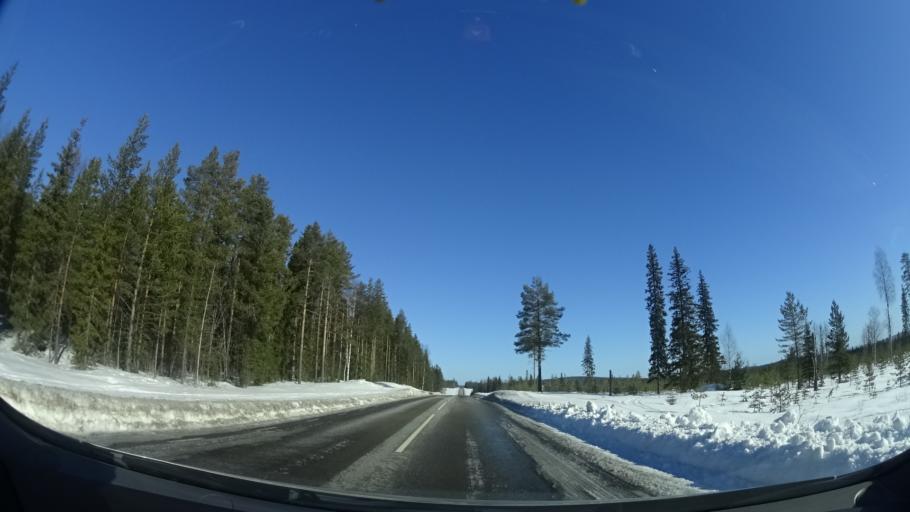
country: SE
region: Vaesterbotten
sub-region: Skelleftea Kommun
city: Langsele
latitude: 65.1407
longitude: 20.1689
